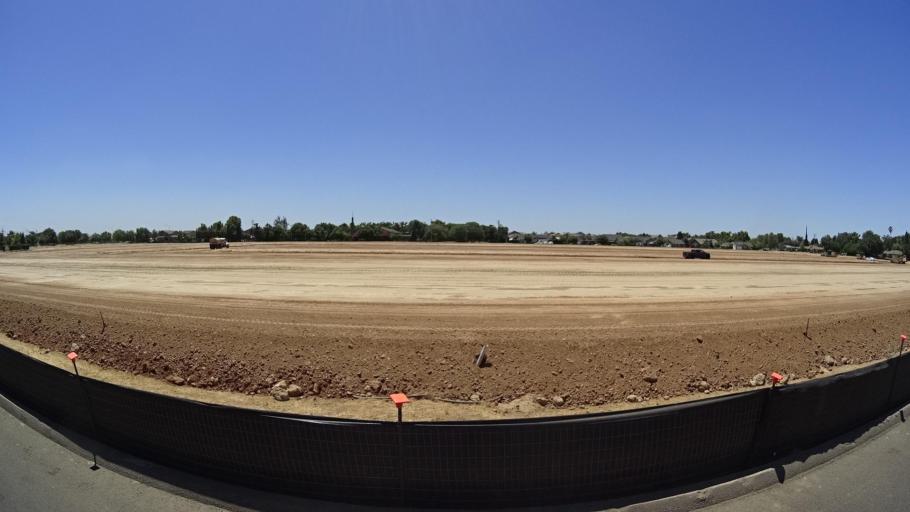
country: US
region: California
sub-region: Fresno County
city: Sunnyside
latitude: 36.7315
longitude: -119.6706
